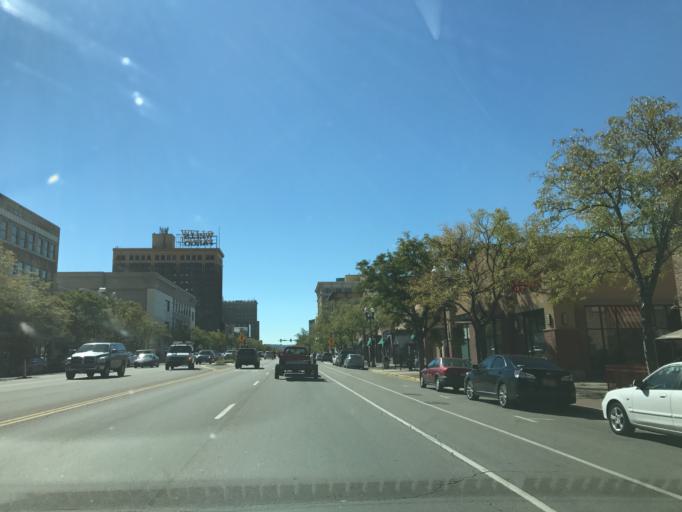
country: US
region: Utah
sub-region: Weber County
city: Ogden
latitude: 41.2247
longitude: -111.9705
